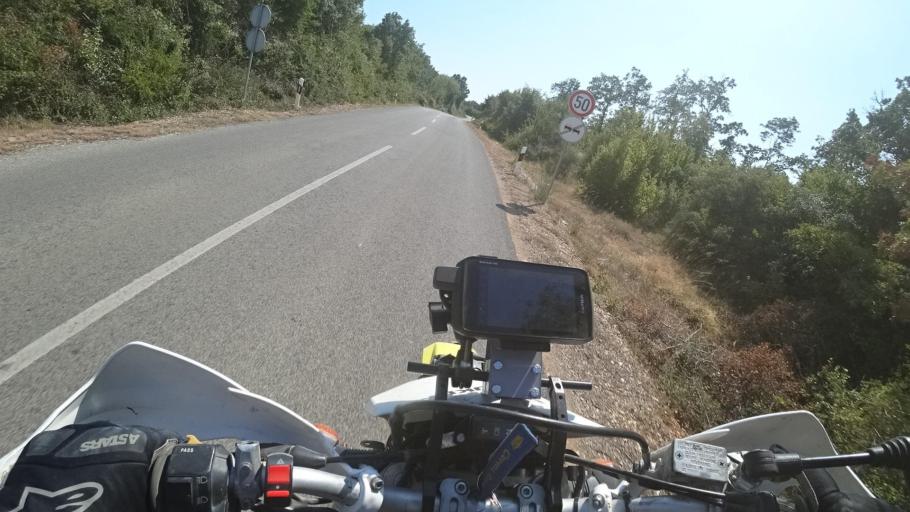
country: HR
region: Istarska
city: Fazana
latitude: 45.0058
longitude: 13.7800
